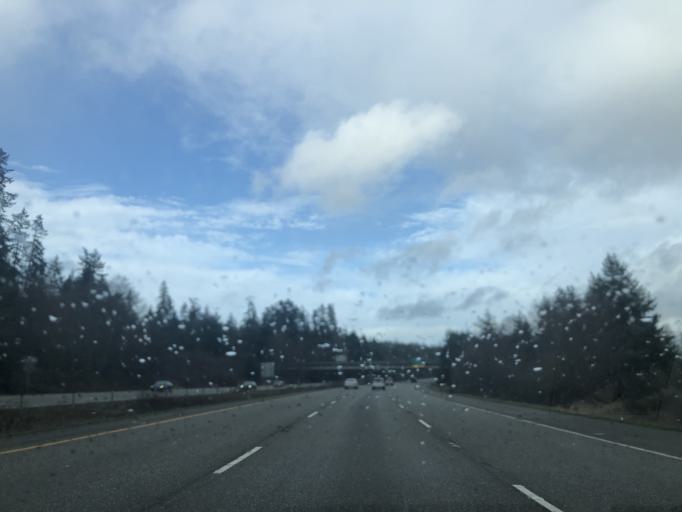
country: US
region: Washington
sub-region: Kitsap County
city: Silverdale
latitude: 47.6763
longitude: -122.6908
